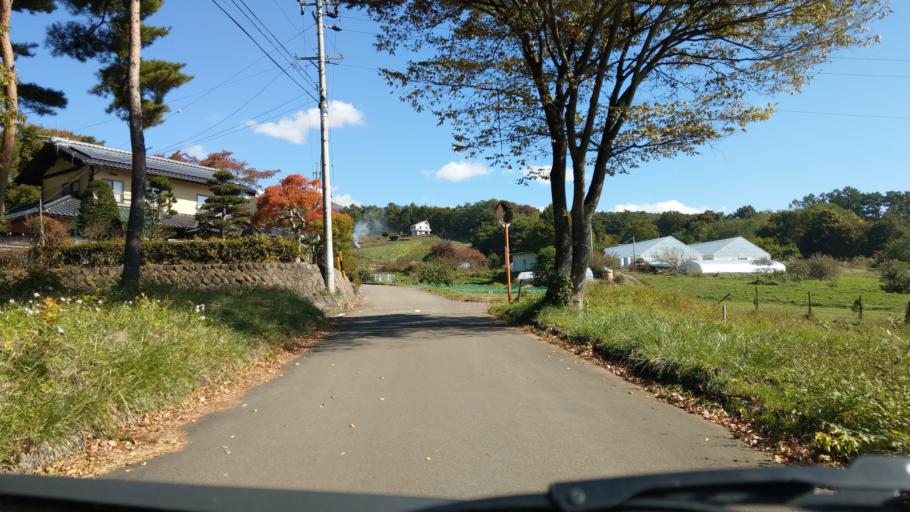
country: JP
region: Nagano
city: Komoro
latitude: 36.3638
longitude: 138.4039
